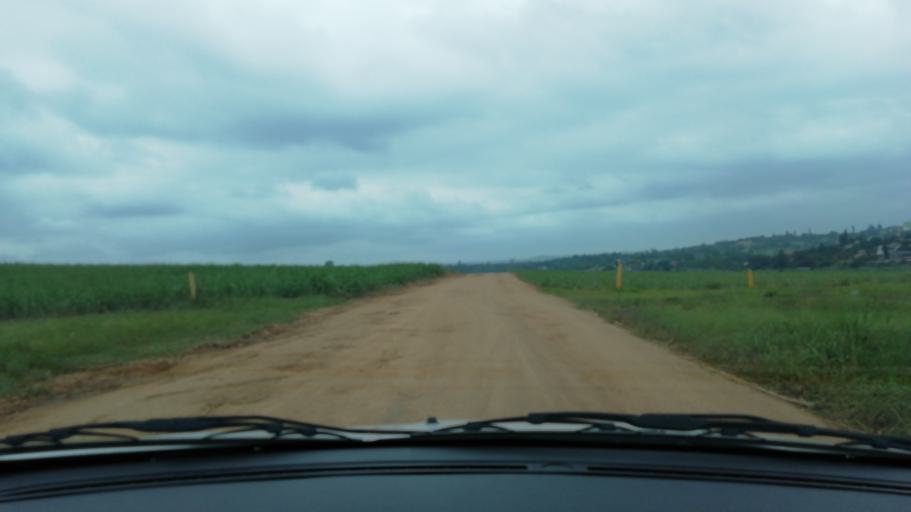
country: ZA
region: KwaZulu-Natal
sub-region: uThungulu District Municipality
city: Empangeni
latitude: -28.7305
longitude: 31.9080
